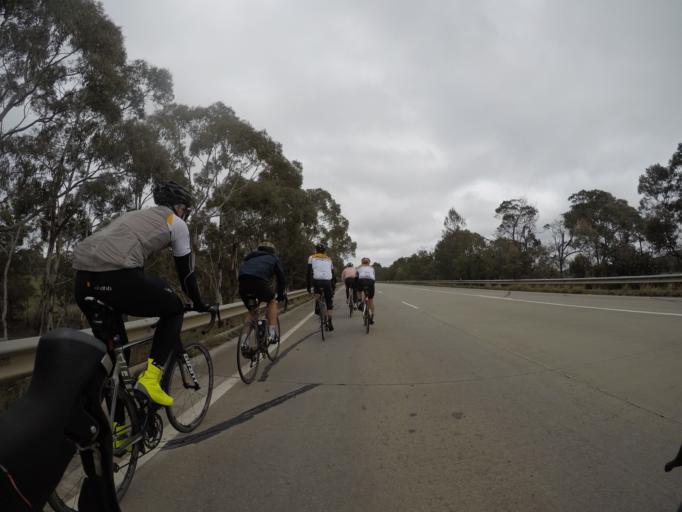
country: AU
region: New South Wales
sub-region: Lithgow
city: Lithgow
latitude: -33.4467
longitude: 150.0392
